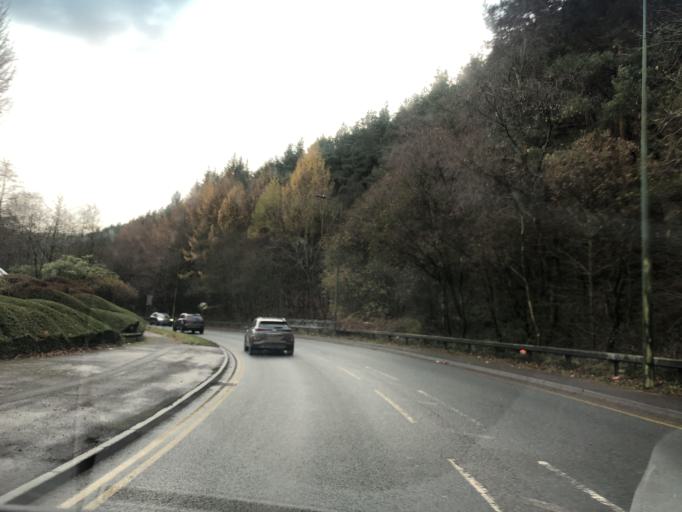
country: GB
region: Wales
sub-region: Blaenau Gwent
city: Abertillery
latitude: 51.7292
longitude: -3.1381
